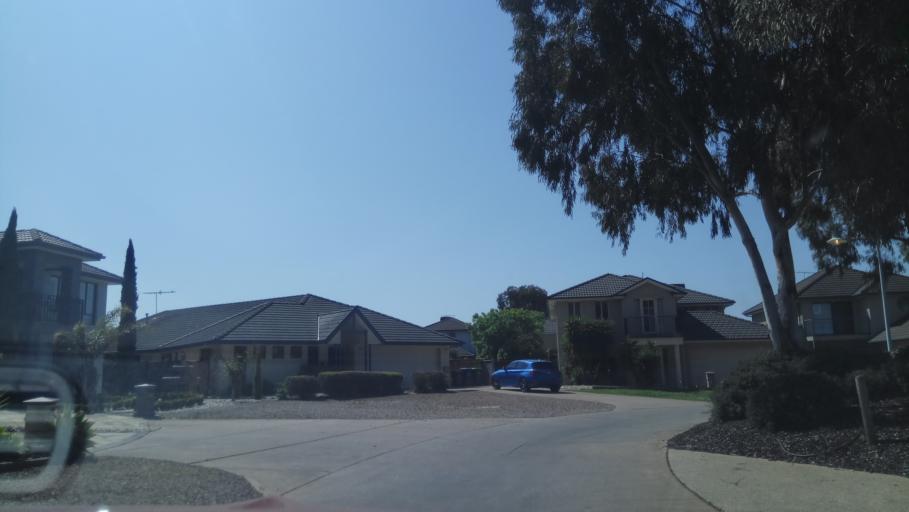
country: AU
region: Victoria
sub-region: Hobsons Bay
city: Altona Meadows
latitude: -37.8857
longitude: 144.7634
